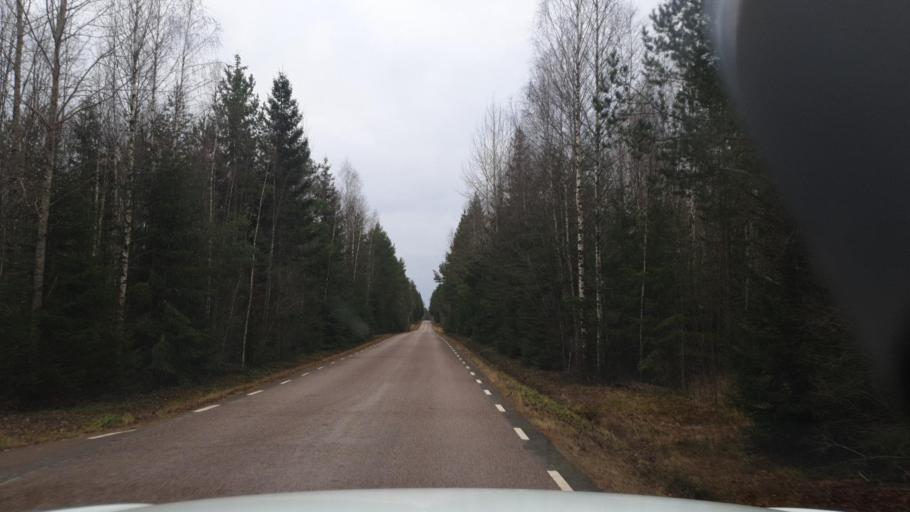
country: SE
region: Vaermland
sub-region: Karlstads Kommun
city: Edsvalla
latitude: 59.5044
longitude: 13.1095
